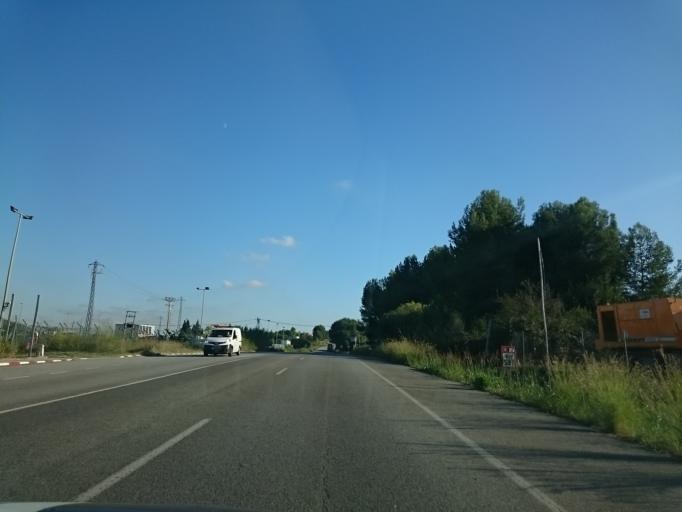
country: ES
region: Catalonia
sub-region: Provincia de Barcelona
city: Palleja
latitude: 41.4322
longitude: 1.9942
